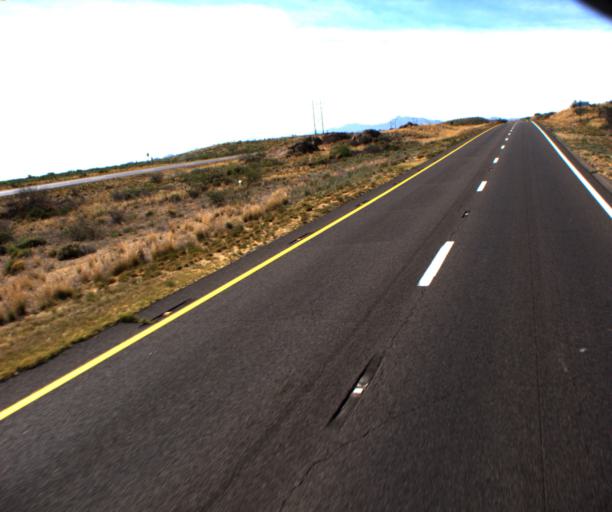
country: US
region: Arizona
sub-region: Graham County
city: Swift Trail Junction
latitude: 32.5215
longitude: -109.6741
